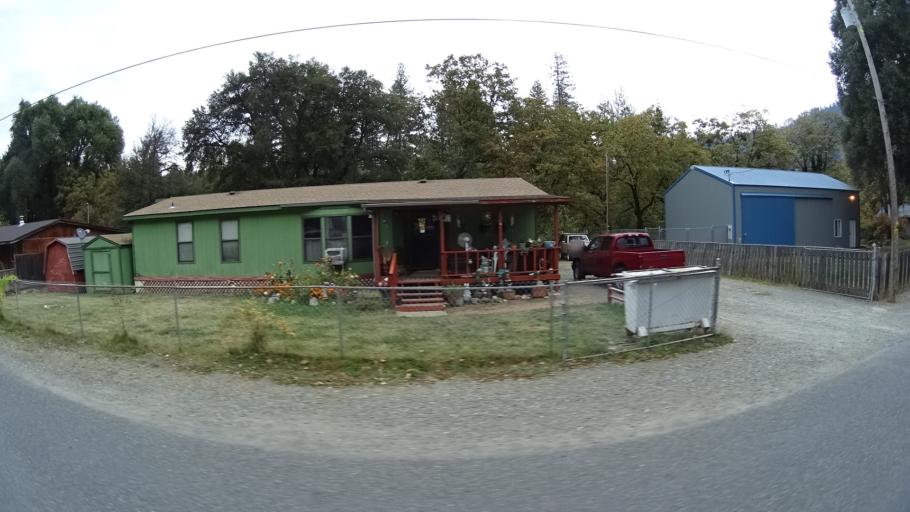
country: US
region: California
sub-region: Siskiyou County
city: Happy Camp
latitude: 41.7977
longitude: -123.3798
